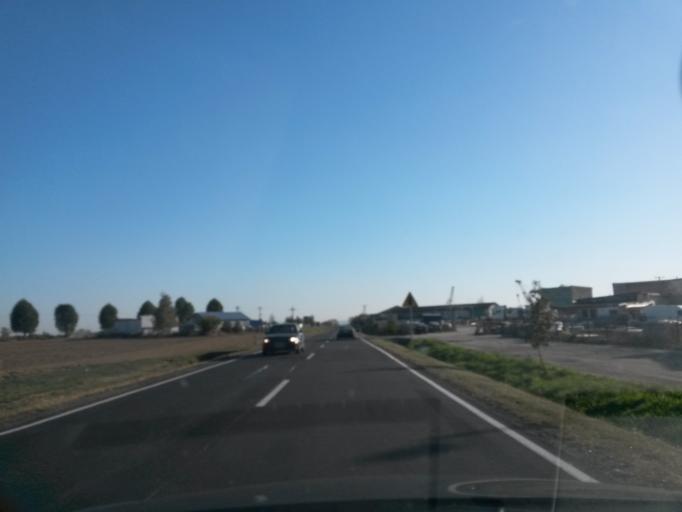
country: PL
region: Lower Silesian Voivodeship
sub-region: Powiat swidnicki
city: Strzegom
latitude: 50.9721
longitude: 16.3665
